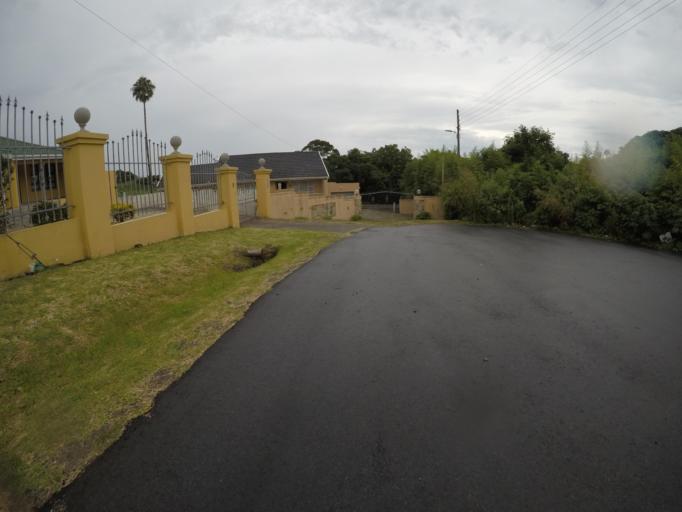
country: ZA
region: Eastern Cape
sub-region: Buffalo City Metropolitan Municipality
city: East London
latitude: -32.9894
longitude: 27.8607
